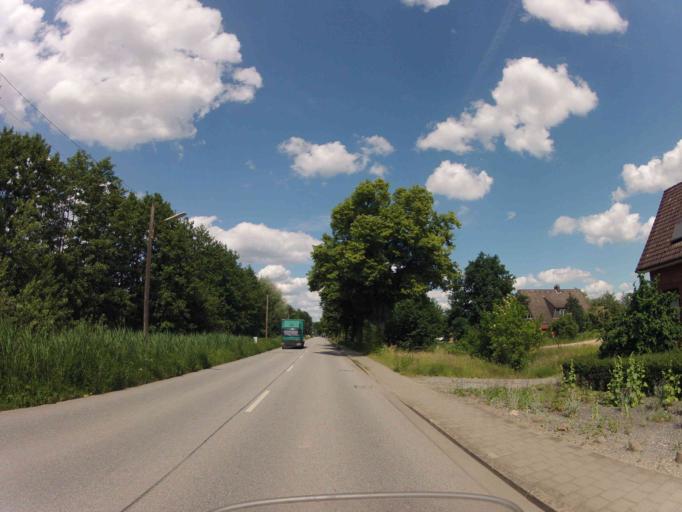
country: DE
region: Lower Saxony
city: Winsen
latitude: 53.4142
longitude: 10.1932
